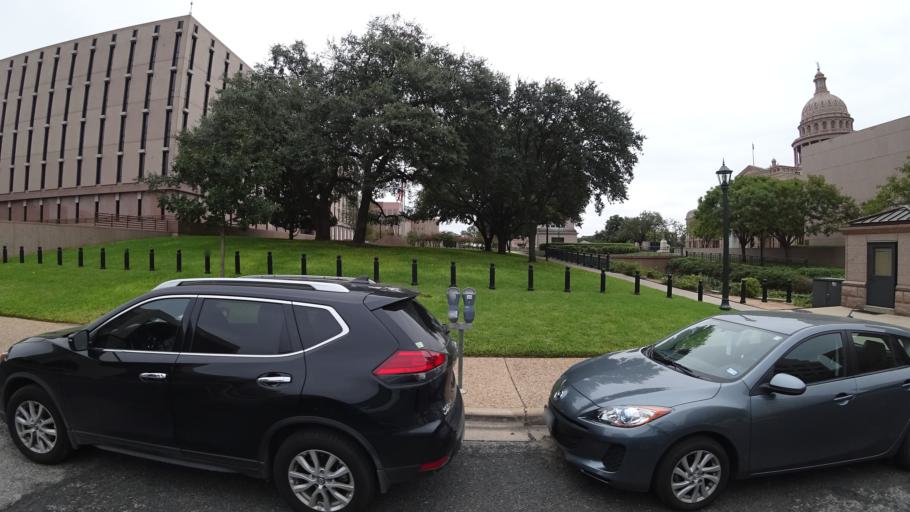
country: US
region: Texas
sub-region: Travis County
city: Austin
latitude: 30.2765
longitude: -97.7411
